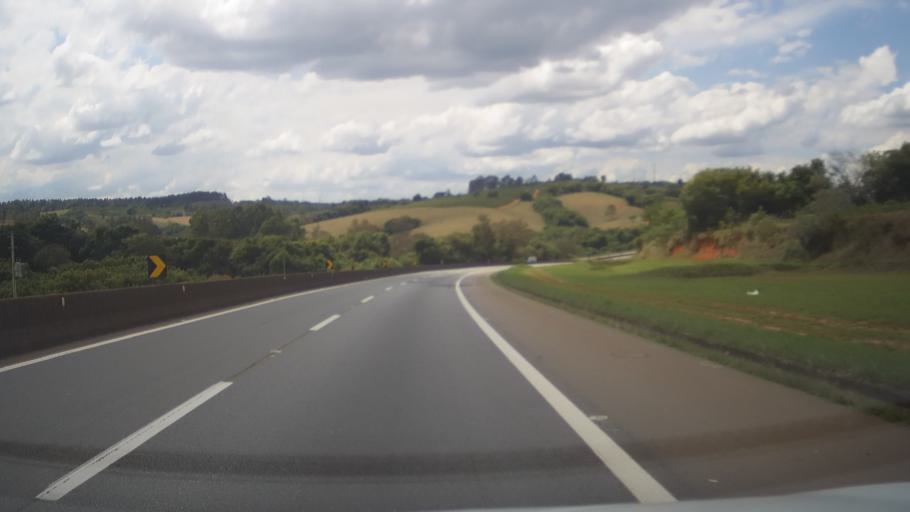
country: BR
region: Minas Gerais
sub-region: Nepomuceno
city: Nepomuceno
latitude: -21.2624
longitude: -45.1394
